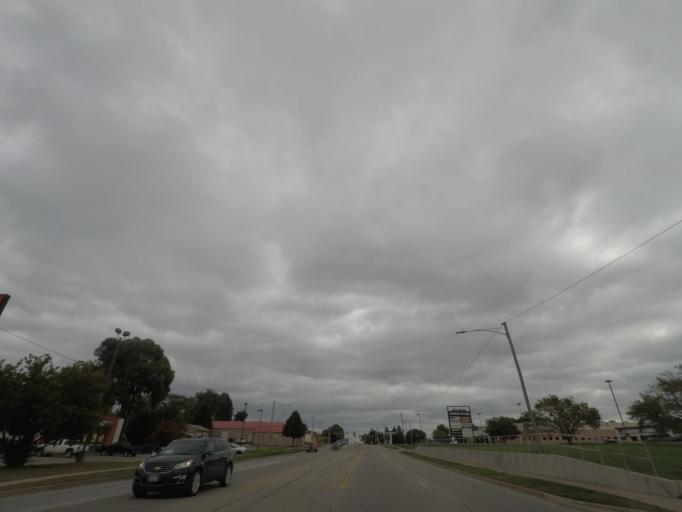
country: US
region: Iowa
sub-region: Polk County
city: Des Moines
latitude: 41.5264
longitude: -93.6191
